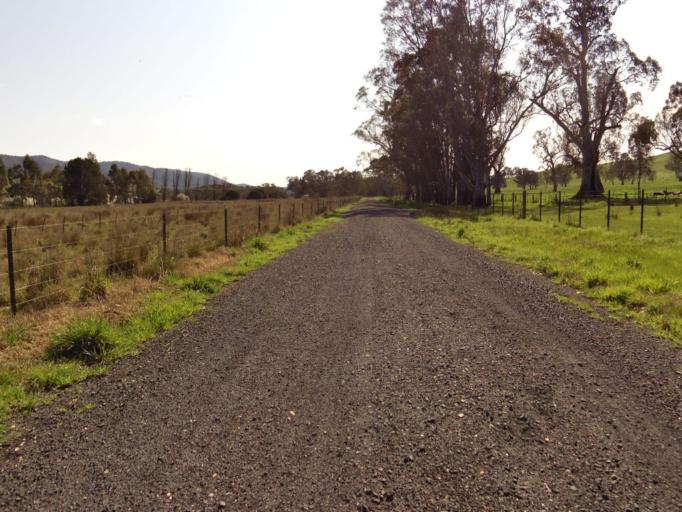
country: AU
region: Victoria
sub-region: Murrindindi
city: Alexandra
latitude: -37.1460
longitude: 145.5881
